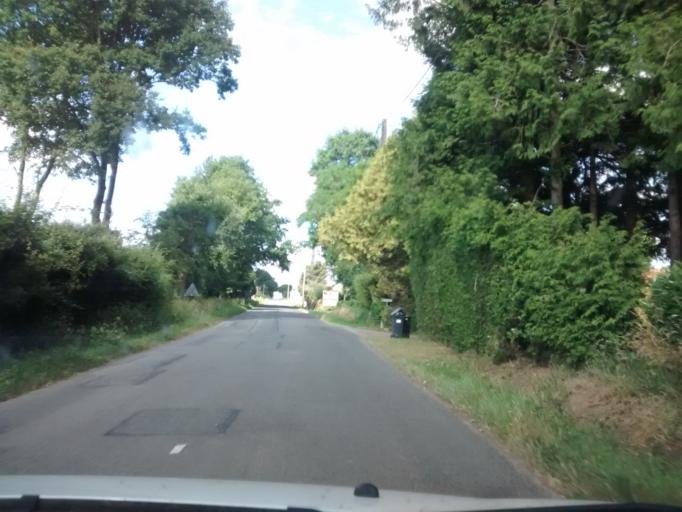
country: FR
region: Brittany
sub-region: Departement d'Ille-et-Vilaine
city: Bain-de-Bretagne
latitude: 47.8308
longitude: -1.6952
